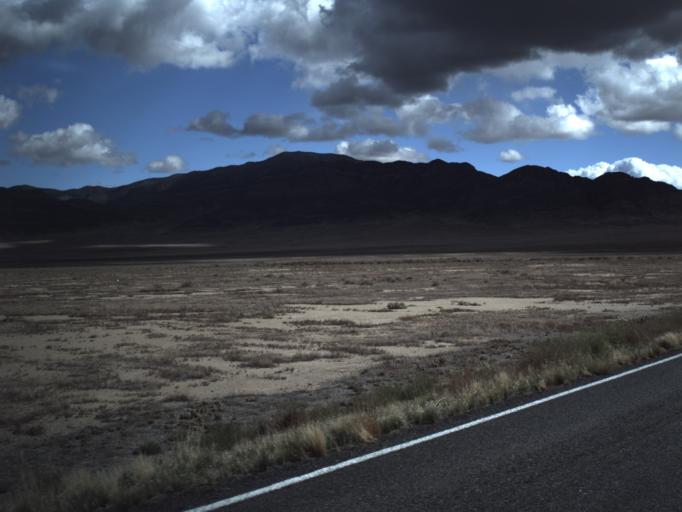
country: US
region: Utah
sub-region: Beaver County
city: Milford
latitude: 38.5245
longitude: -113.6607
